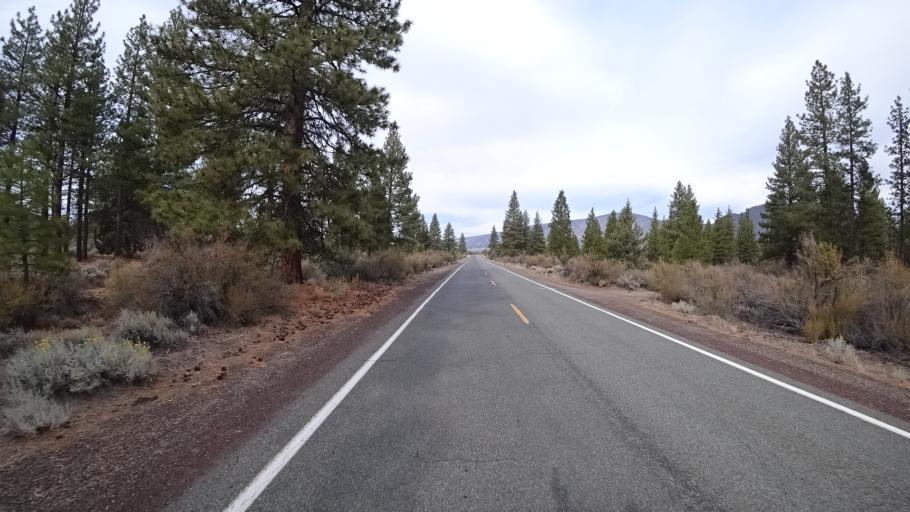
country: US
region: California
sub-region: Siskiyou County
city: Weed
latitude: 41.5461
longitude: -122.2475
